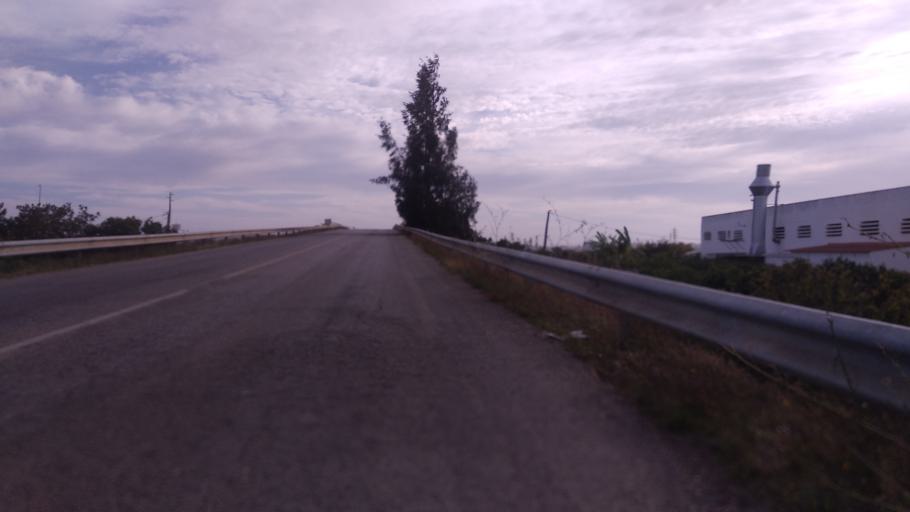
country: PT
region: Faro
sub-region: Faro
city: Faro
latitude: 37.0431
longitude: -7.9381
